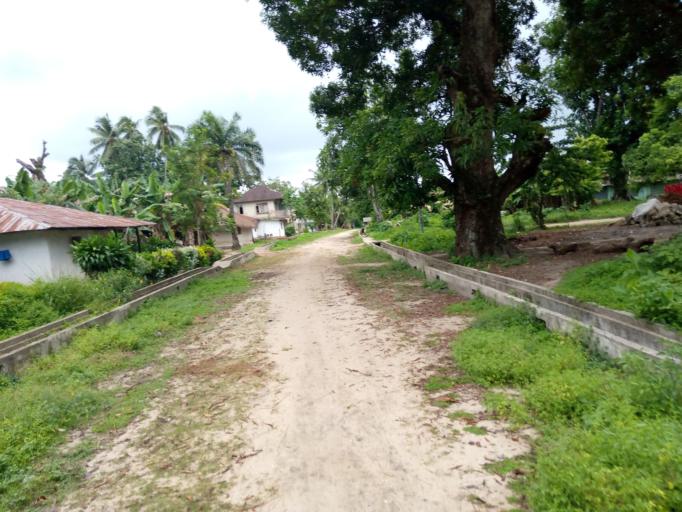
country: SL
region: Southern Province
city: Bonthe
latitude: 7.5334
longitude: -12.5036
